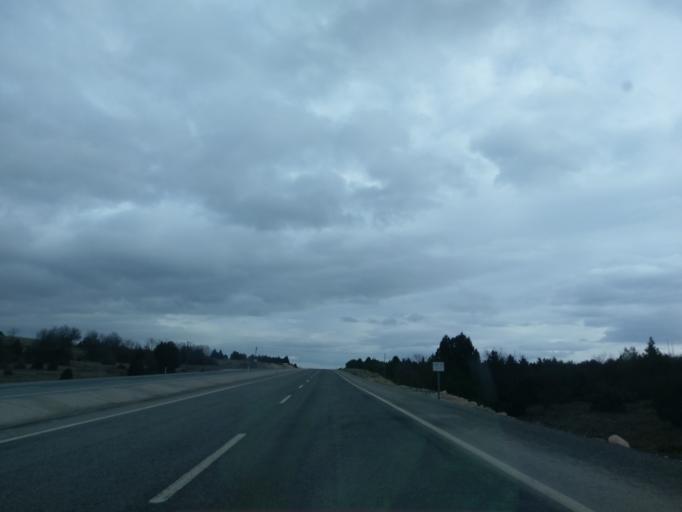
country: TR
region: Kuetahya
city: Aslanapa
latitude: 39.2253
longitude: 29.7547
